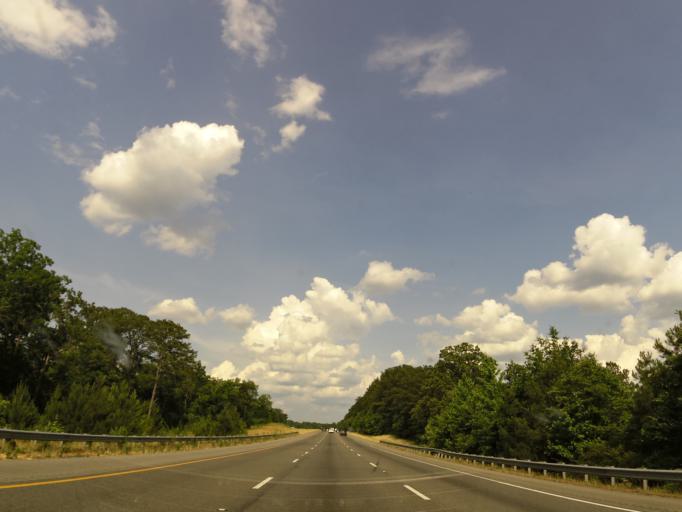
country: US
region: Alabama
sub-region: Tuscaloosa County
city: Coaling
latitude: 33.1833
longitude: -87.3544
